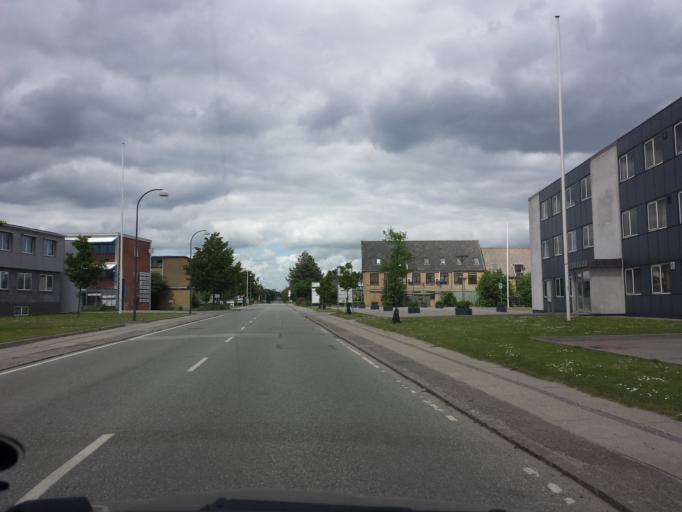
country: DK
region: Capital Region
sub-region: Herlev Kommune
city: Herlev
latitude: 55.7147
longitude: 12.4294
